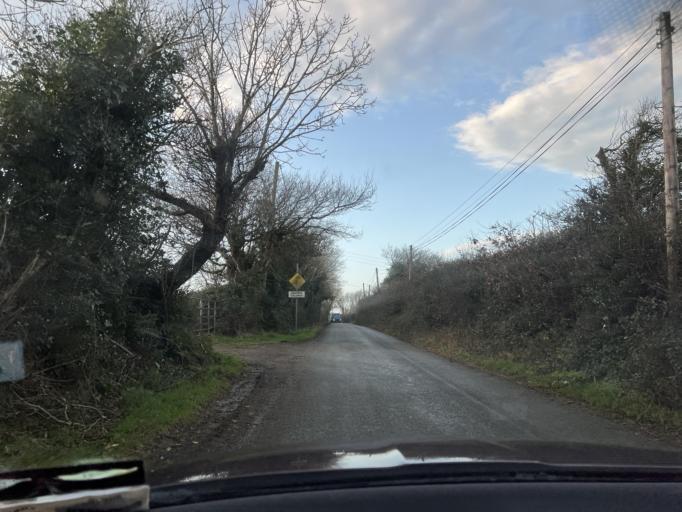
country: IE
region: Leinster
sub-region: Loch Garman
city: Loch Garman
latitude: 52.3625
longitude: -6.5247
